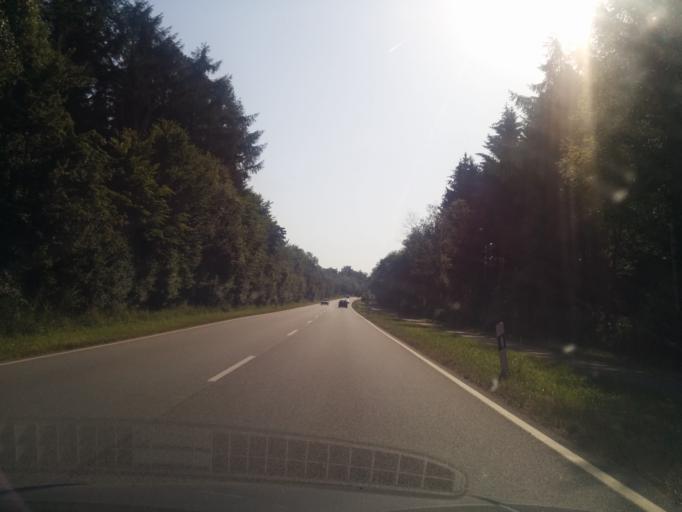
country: DE
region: Bavaria
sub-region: Upper Bavaria
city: Oberhaching
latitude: 48.0342
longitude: 11.5641
